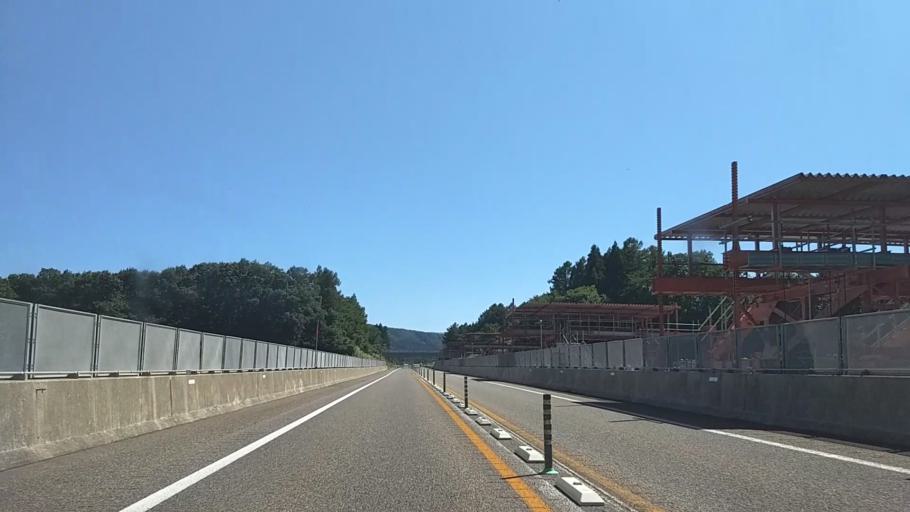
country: JP
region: Niigata
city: Arai
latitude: 36.9865
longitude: 138.2133
